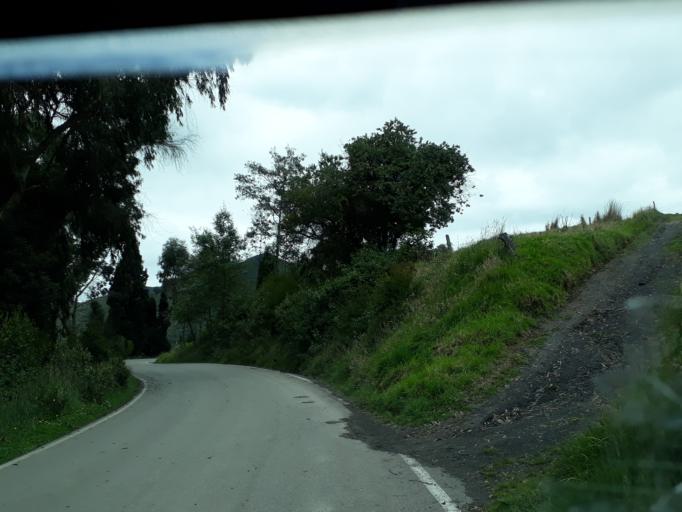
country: CO
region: Cundinamarca
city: Sutatausa
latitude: 5.2012
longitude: -73.8974
